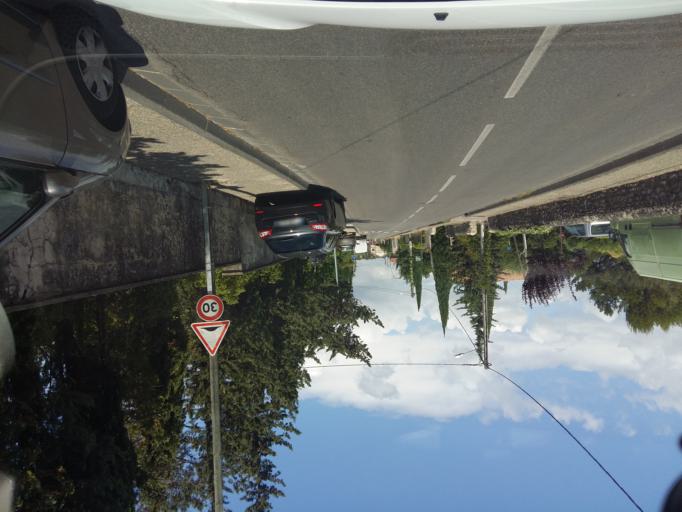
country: FR
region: Provence-Alpes-Cote d'Azur
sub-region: Departement du Vaucluse
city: Vaison-la-Romaine
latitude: 44.2455
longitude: 5.0691
